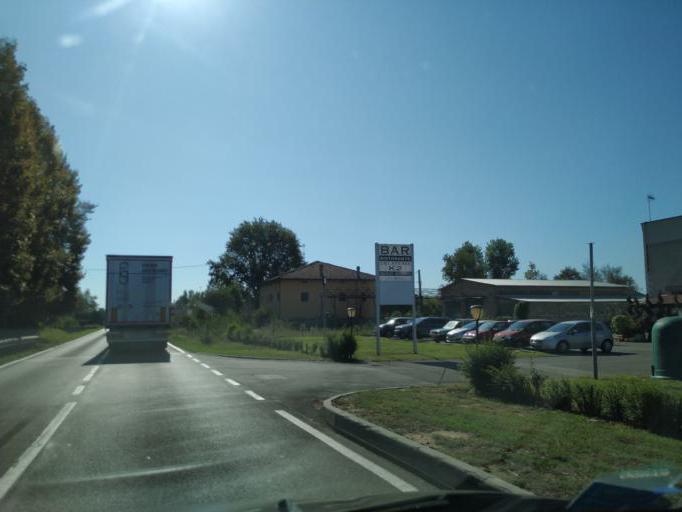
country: IT
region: Emilia-Romagna
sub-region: Provincia di Bologna
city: Sant'Agata Bolognese
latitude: 44.6572
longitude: 11.1339
